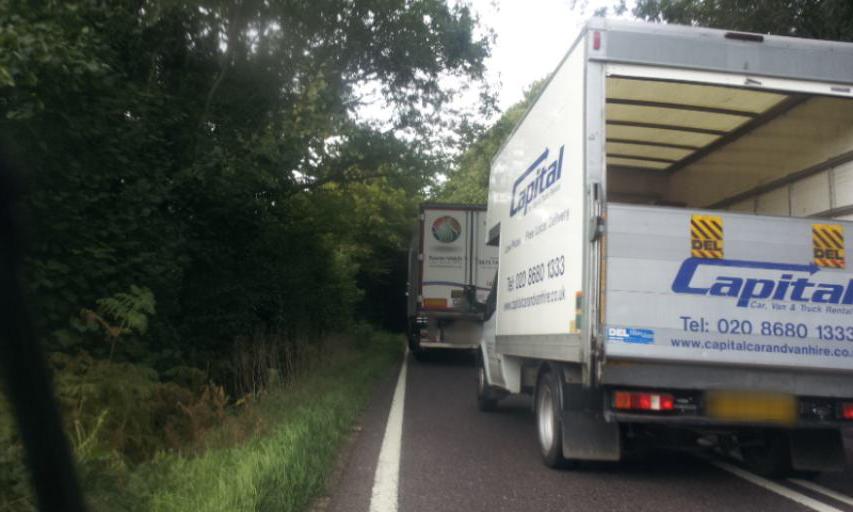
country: GB
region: England
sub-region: Kent
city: Kings Hill
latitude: 51.2631
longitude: 0.3627
